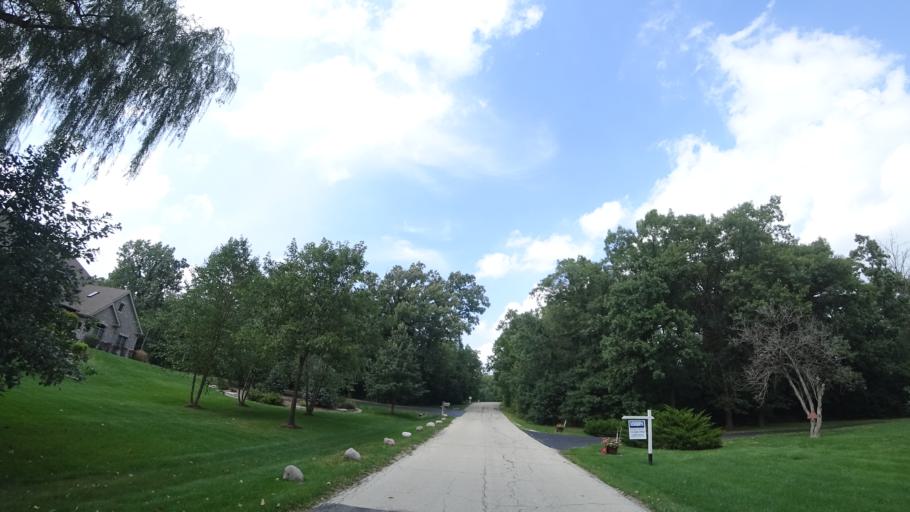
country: US
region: Illinois
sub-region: Will County
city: Goodings Grove
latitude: 41.6592
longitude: -87.9015
